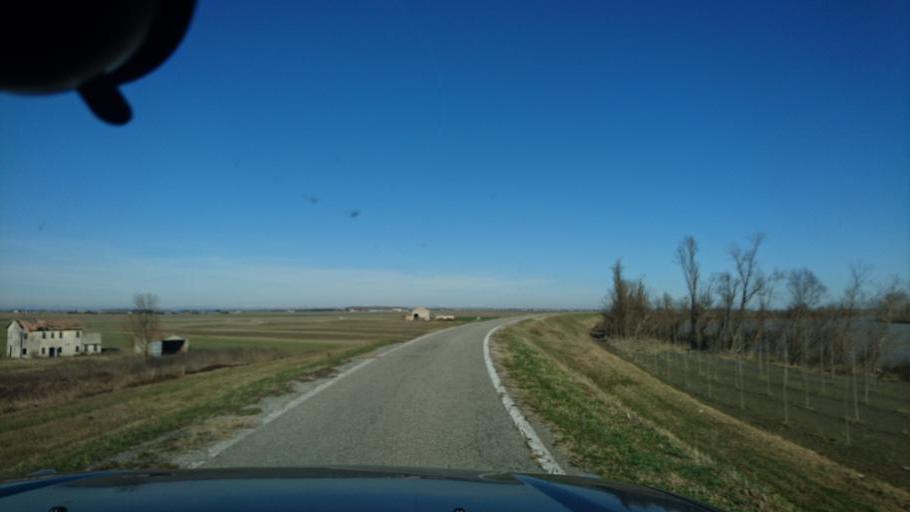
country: IT
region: Veneto
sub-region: Provincia di Rovigo
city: Ariano
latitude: 44.9353
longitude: 12.1575
